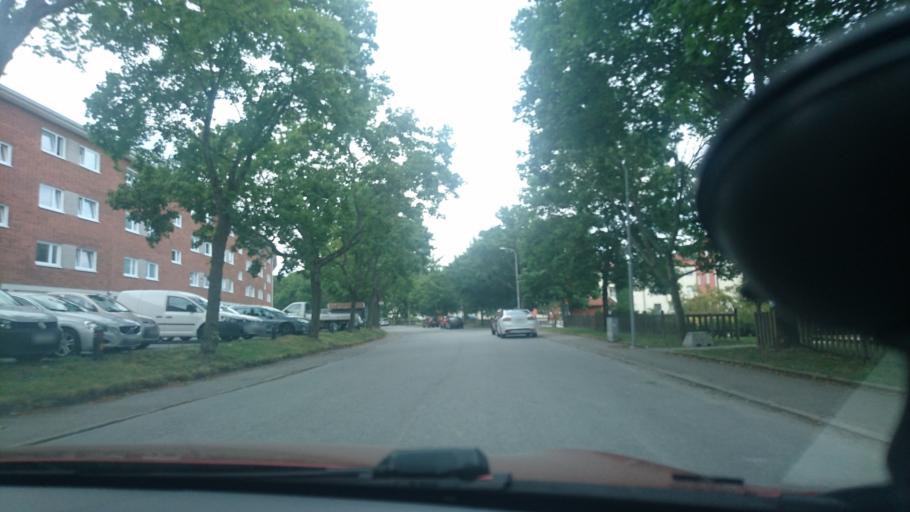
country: SE
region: Stockholm
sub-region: Upplands Vasby Kommun
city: Upplands Vaesby
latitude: 59.5209
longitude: 17.8945
